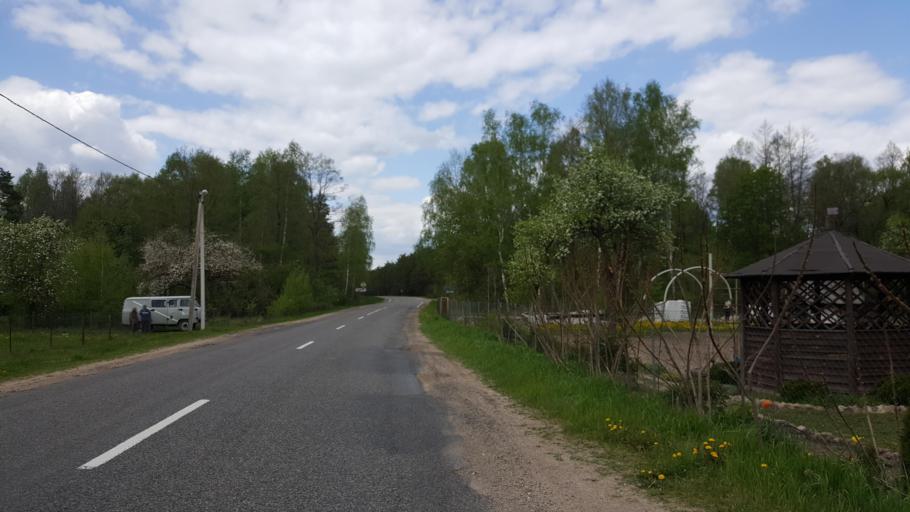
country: BY
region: Brest
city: Zhabinka
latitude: 52.3963
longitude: 24.0909
